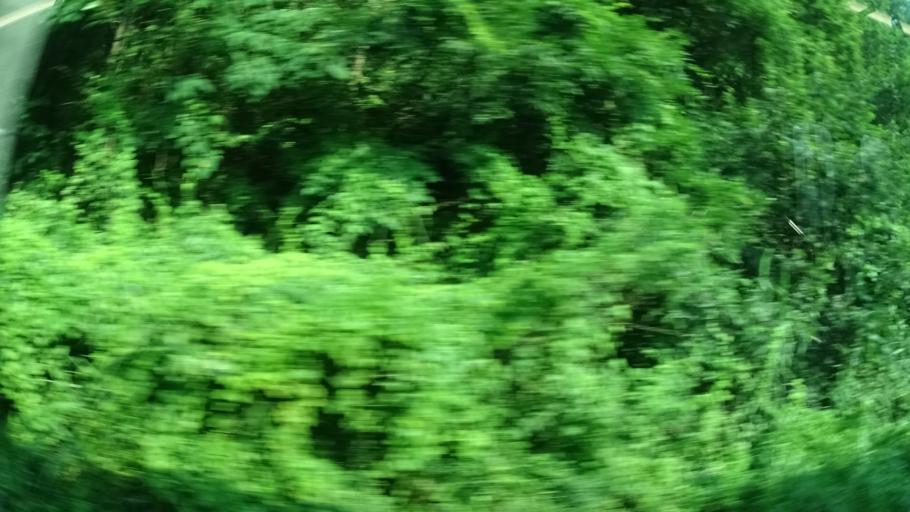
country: JP
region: Fukushima
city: Iwaki
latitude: 36.9506
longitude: 140.8395
